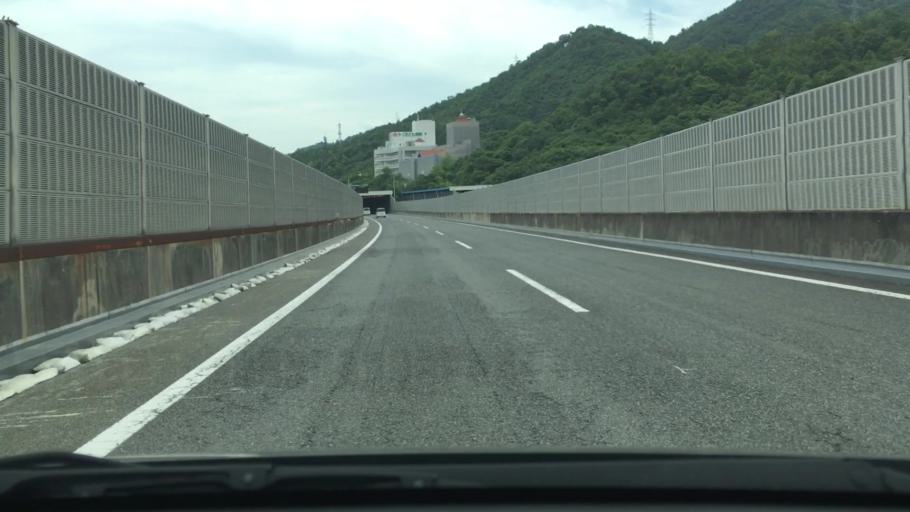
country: JP
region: Hiroshima
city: Ono-hara
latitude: 34.2594
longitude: 132.2266
